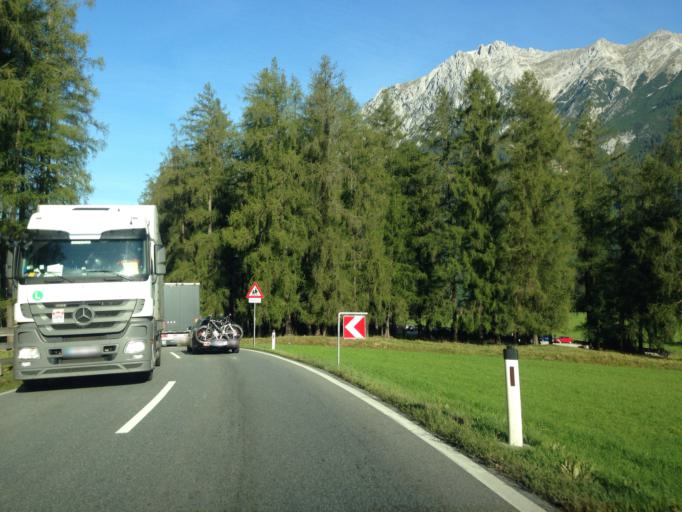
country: AT
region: Tyrol
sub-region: Politischer Bezirk Imst
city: Obsteig
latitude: 47.3081
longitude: 10.8874
